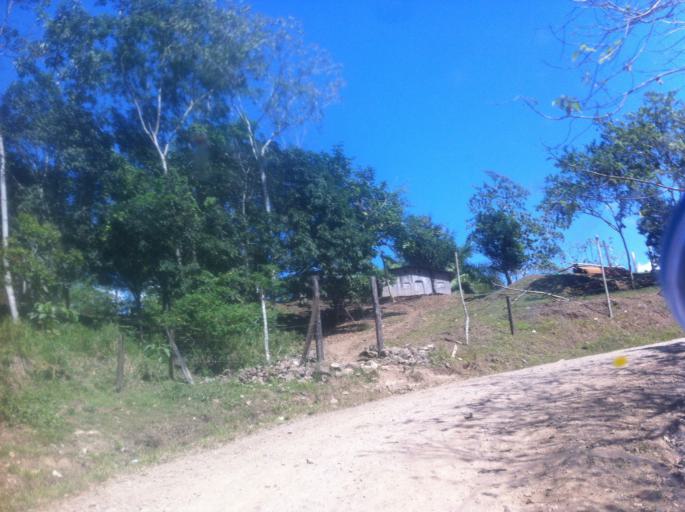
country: CR
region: Alajuela
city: Los Chiles
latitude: 11.2503
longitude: -84.4448
